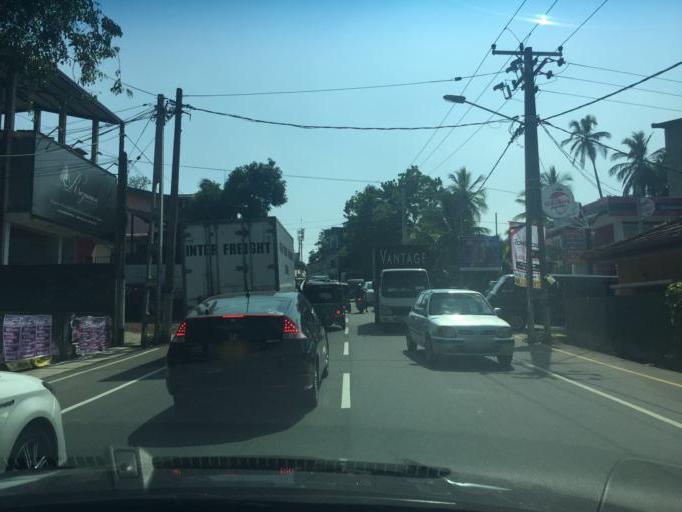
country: LK
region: Western
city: Sri Jayewardenepura Kotte
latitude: 6.8634
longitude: 79.8957
